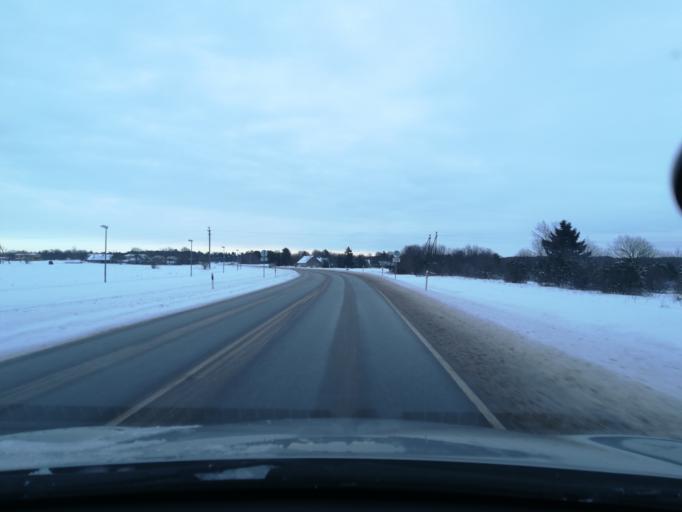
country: EE
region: Harju
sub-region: Harku vald
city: Tabasalu
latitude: 59.4439
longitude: 24.4841
